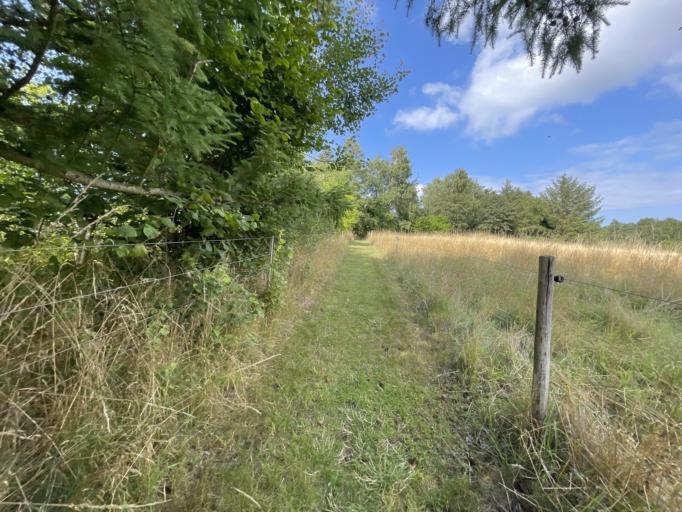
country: DK
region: Capital Region
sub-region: Gribskov Kommune
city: Helsinge
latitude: 56.0914
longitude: 12.1792
